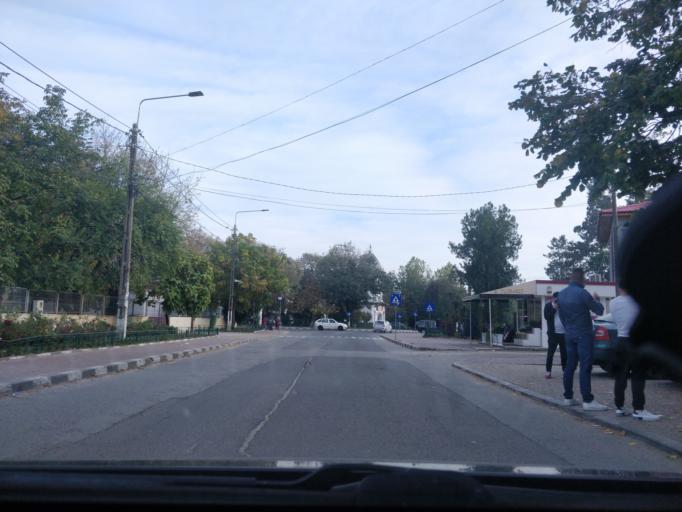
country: RO
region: Giurgiu
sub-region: Comuna Bolintin Vale
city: Bolintin Vale
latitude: 44.4469
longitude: 25.7567
